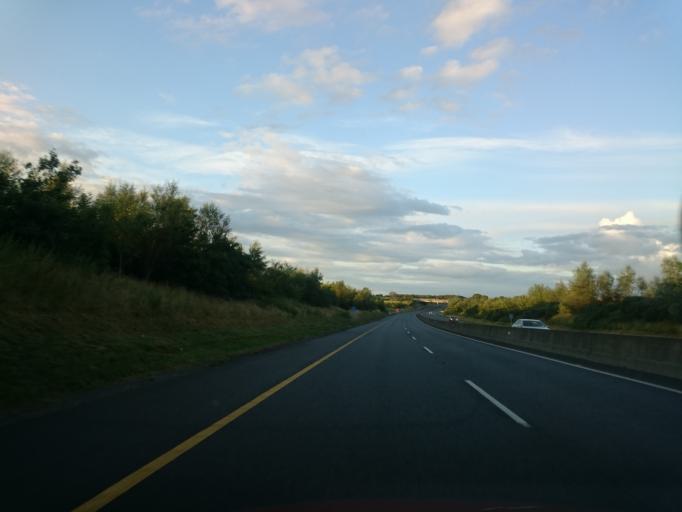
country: IE
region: Leinster
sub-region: Loch Garman
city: Castletown
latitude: 52.7374
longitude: -6.2319
